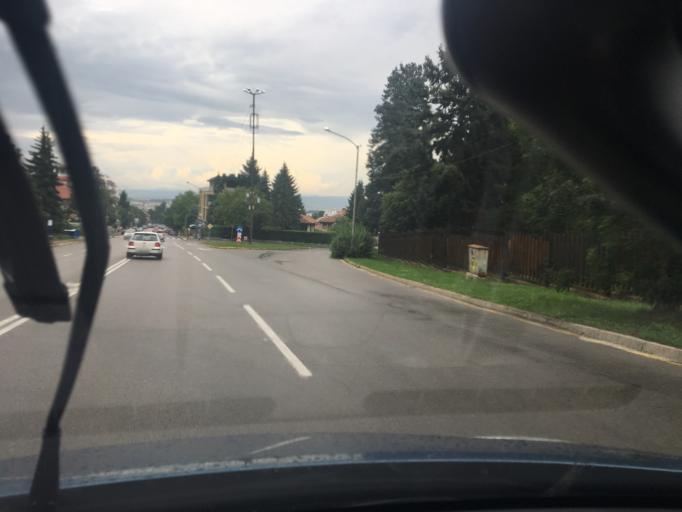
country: BG
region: Sofia-Capital
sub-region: Stolichna Obshtina
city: Sofia
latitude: 42.6544
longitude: 23.2658
